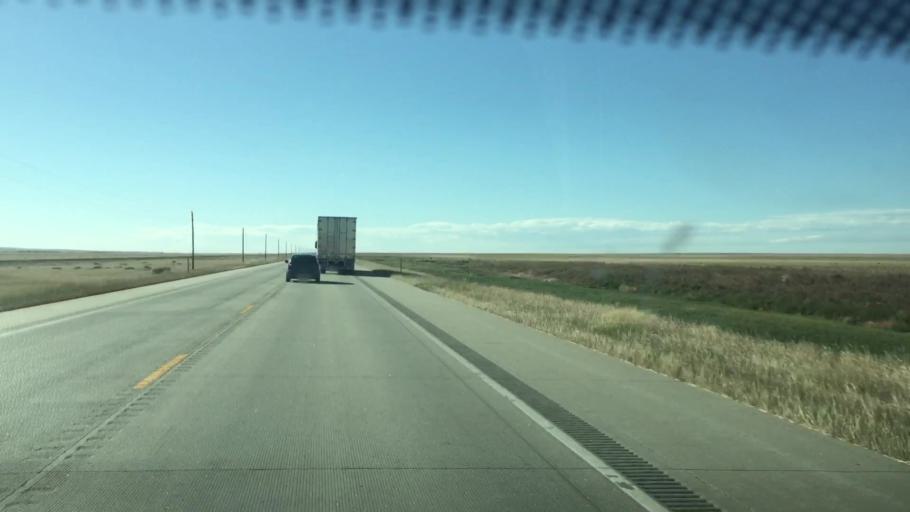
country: US
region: Colorado
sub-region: Kiowa County
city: Eads
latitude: 38.8316
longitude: -103.0468
